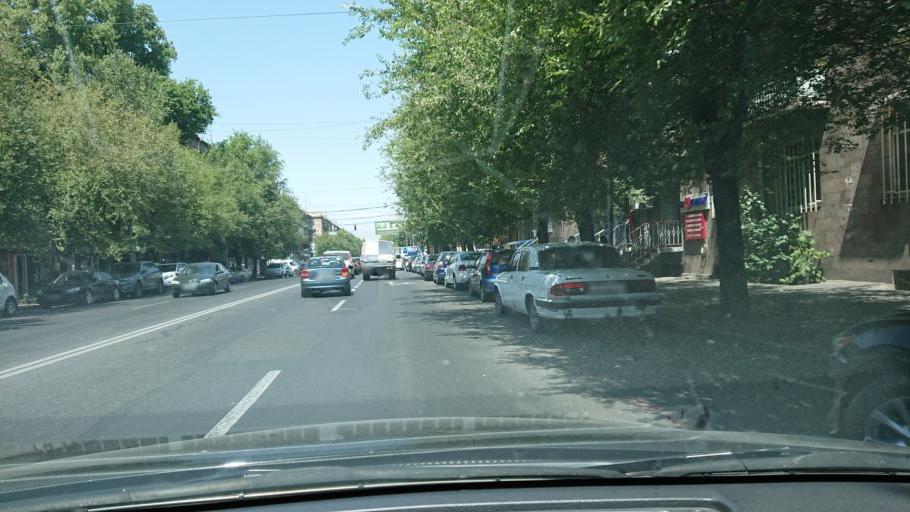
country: AM
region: Yerevan
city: Yerevan
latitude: 40.2020
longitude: 44.4993
